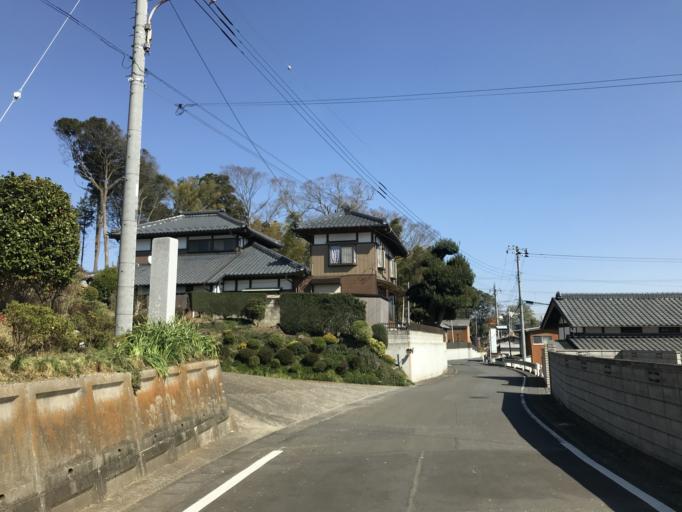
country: JP
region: Ibaraki
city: Moriya
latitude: 35.9604
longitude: 139.9557
